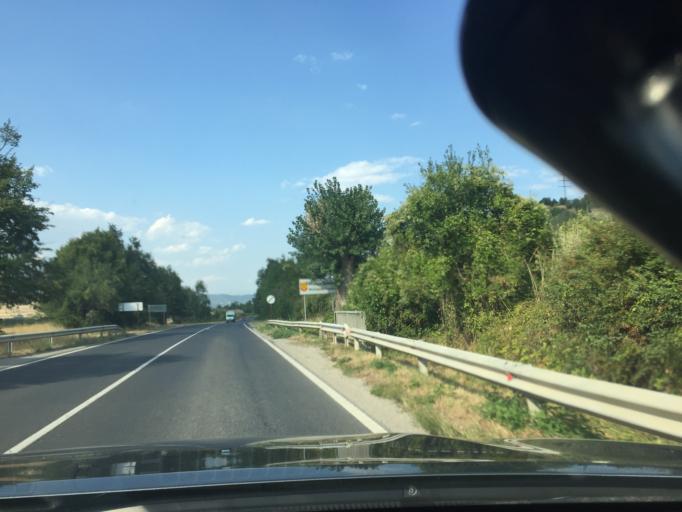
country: BG
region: Kyustendil
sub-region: Obshtina Boboshevo
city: Boboshevo
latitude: 42.1979
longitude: 23.0630
